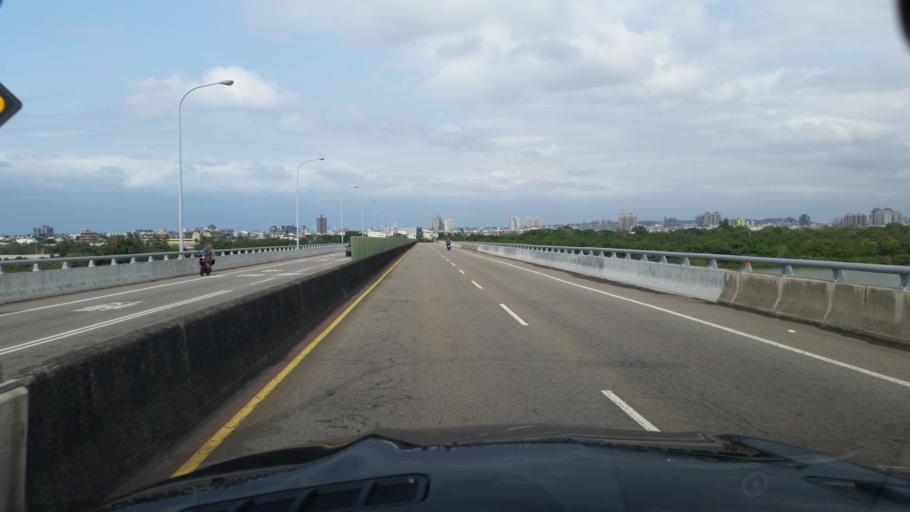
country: TW
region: Taiwan
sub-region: Miaoli
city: Miaoli
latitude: 24.6640
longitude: 120.8669
